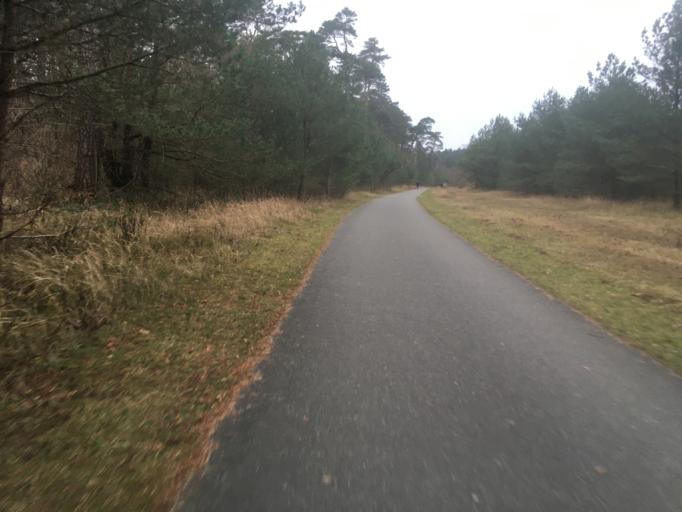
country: DE
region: Mecklenburg-Vorpommern
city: Sagard
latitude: 54.4726
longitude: 13.5679
